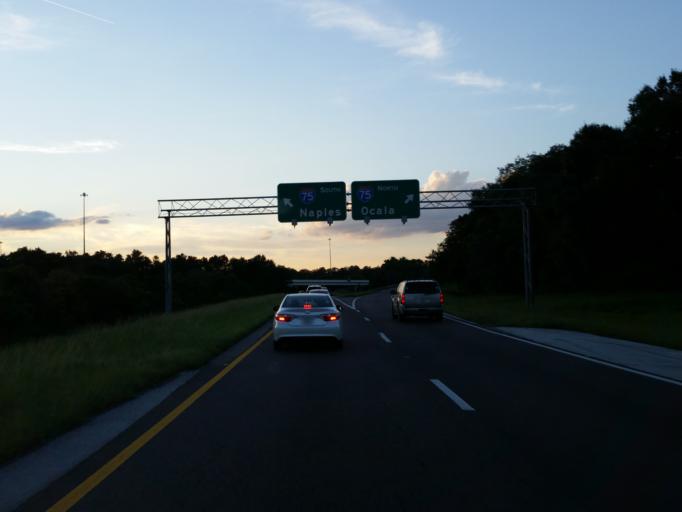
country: US
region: Florida
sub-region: Hillsborough County
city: Mango
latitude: 28.0042
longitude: -82.3245
